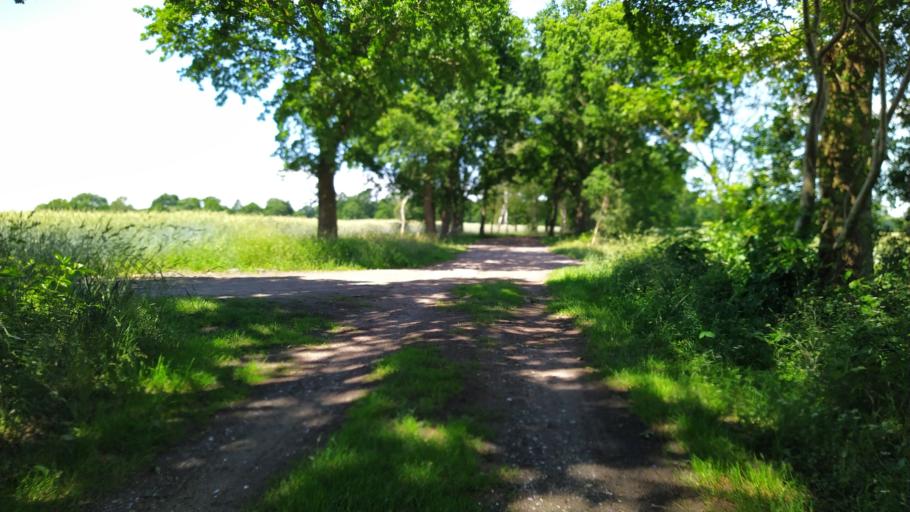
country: DE
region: Lower Saxony
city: Oldendorf
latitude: 53.5649
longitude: 9.2500
